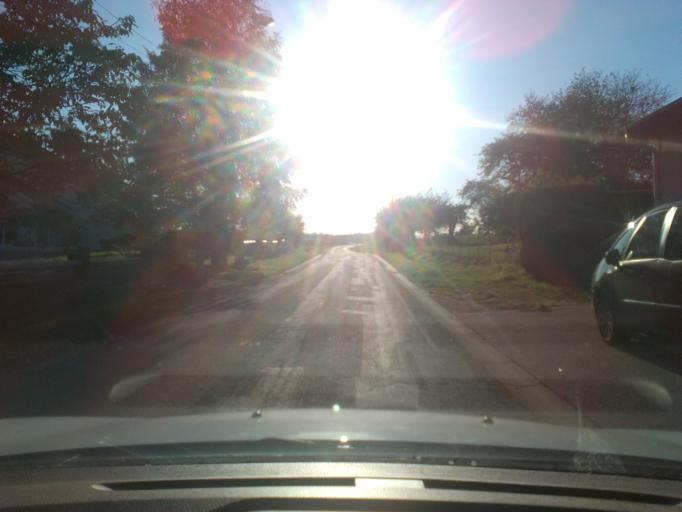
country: FR
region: Lorraine
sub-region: Departement des Vosges
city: Rambervillers
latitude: 48.2893
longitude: 6.6541
